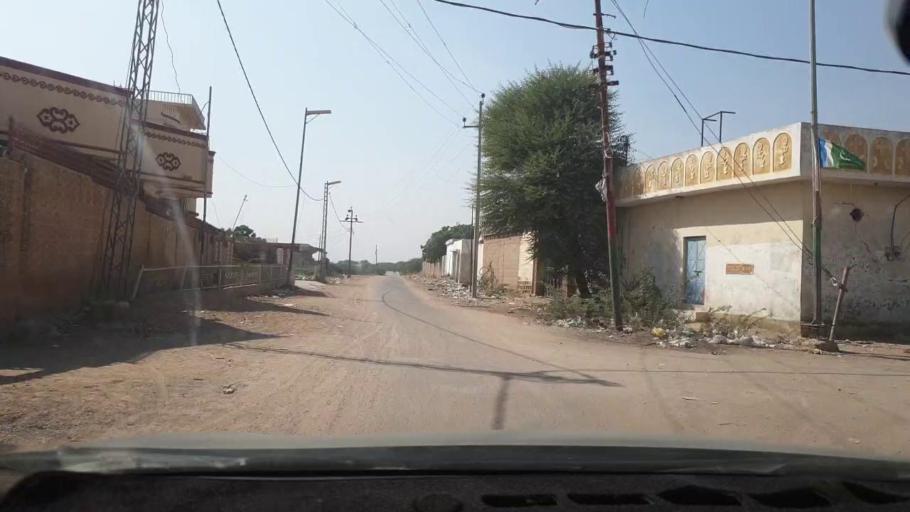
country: PK
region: Sindh
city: Malir Cantonment
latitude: 25.1309
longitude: 67.2312
